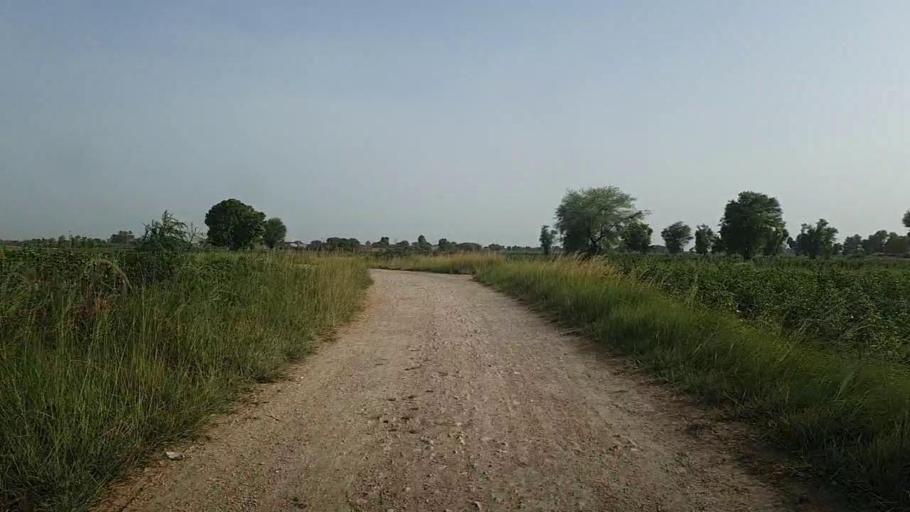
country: PK
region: Sindh
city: Pad Idan
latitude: 26.7540
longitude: 68.2566
